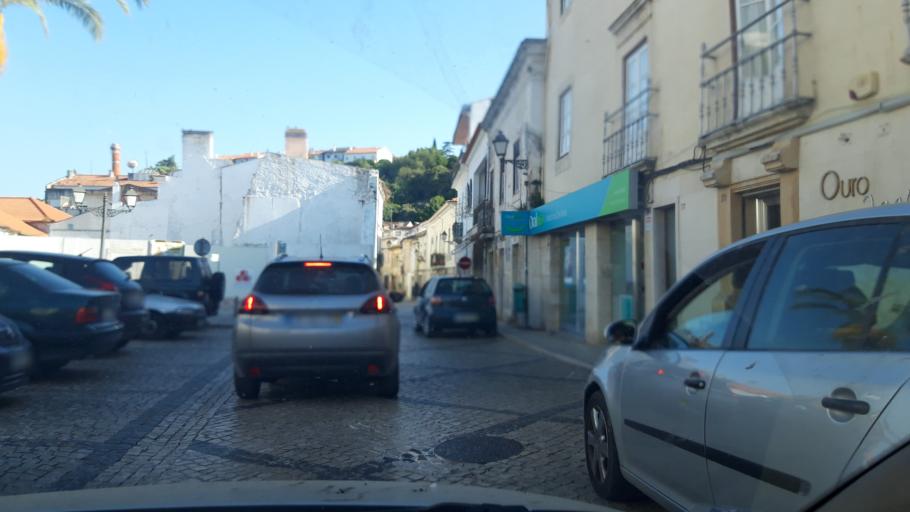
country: PT
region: Santarem
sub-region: Torres Novas
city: Torres Novas
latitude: 39.4779
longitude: -8.5390
